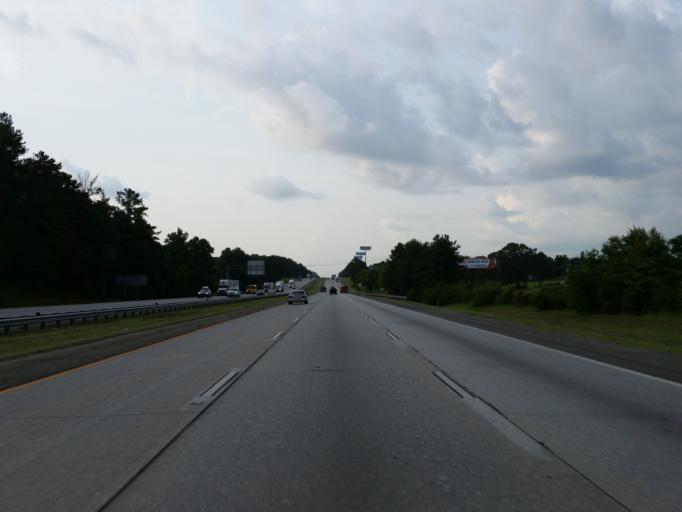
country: US
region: Georgia
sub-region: Peach County
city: Byron
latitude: 32.6205
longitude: -83.7429
